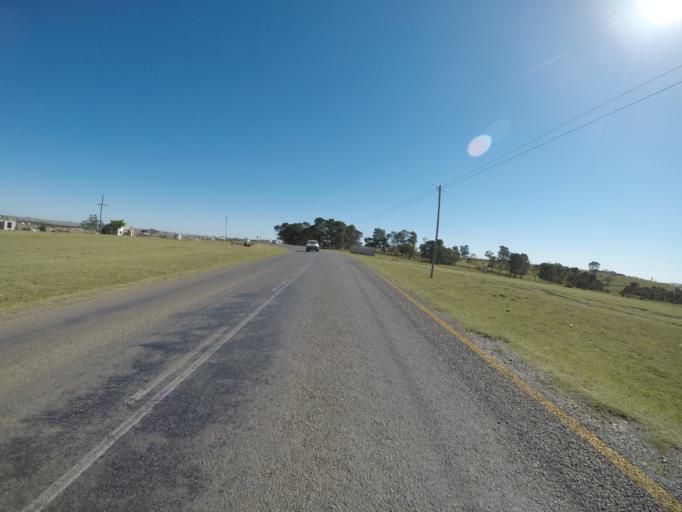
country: ZA
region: Eastern Cape
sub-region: OR Tambo District Municipality
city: Mthatha
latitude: -31.7919
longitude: 28.7452
